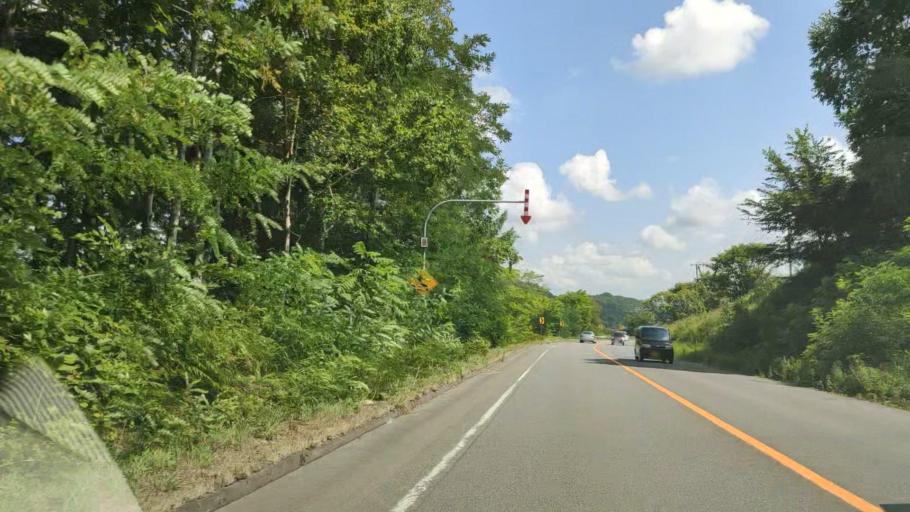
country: JP
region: Hokkaido
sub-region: Asahikawa-shi
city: Asahikawa
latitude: 43.5860
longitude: 142.4443
